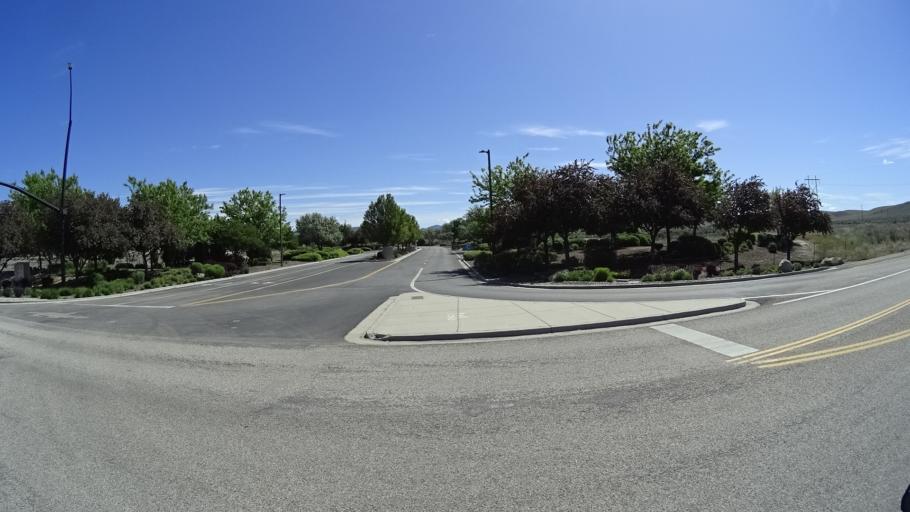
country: US
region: Idaho
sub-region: Ada County
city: Boise
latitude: 43.5179
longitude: -116.1455
